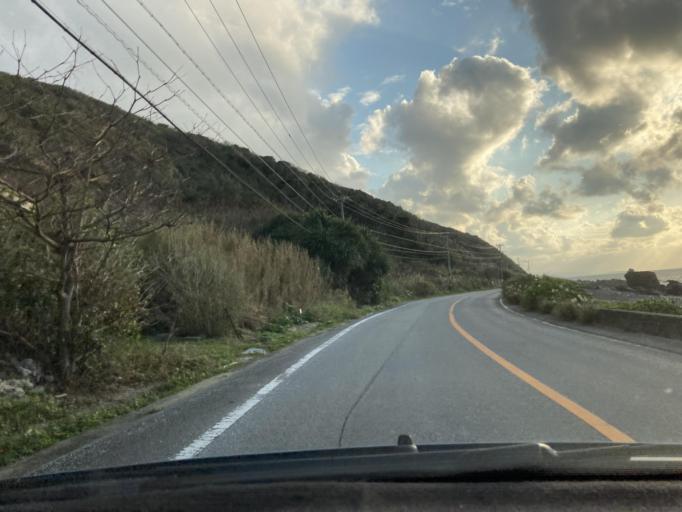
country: JP
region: Okinawa
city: Nago
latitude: 26.8163
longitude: 128.2377
